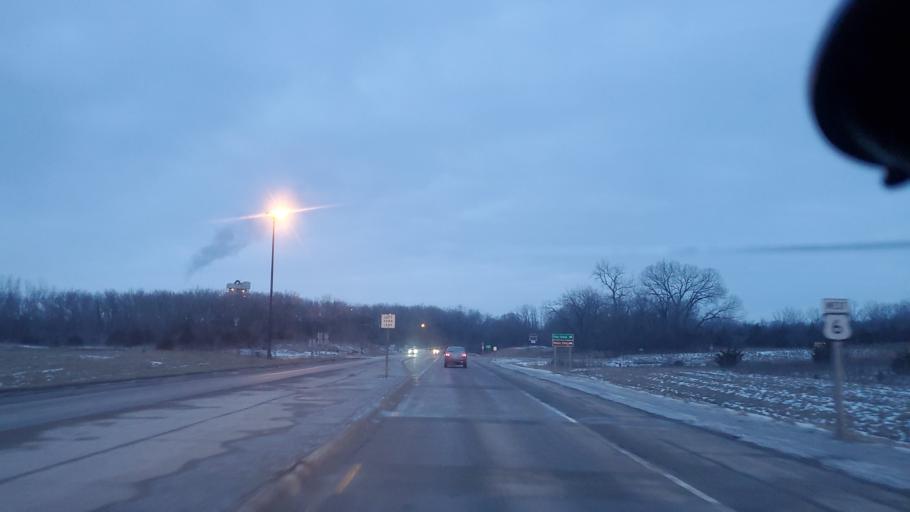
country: US
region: Illinois
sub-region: LaSalle County
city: La Salle
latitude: 41.3355
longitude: -89.0739
